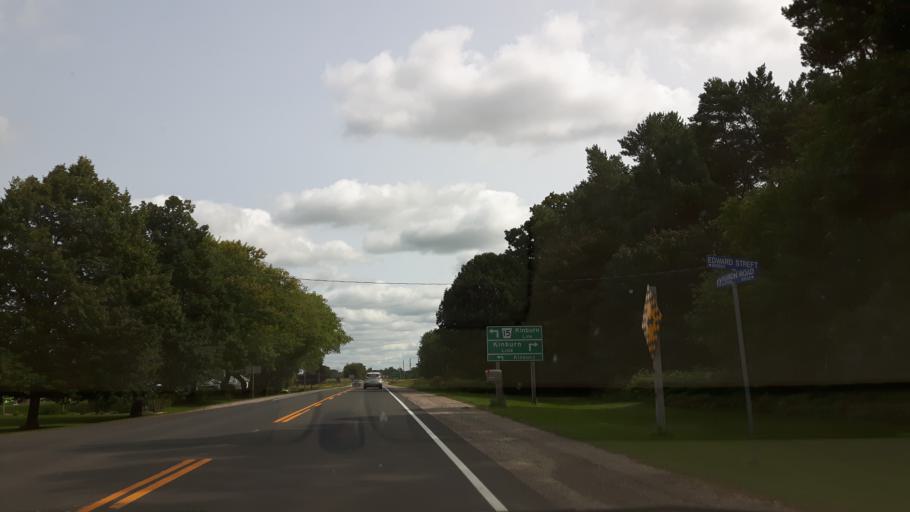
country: CA
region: Ontario
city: Huron East
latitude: 43.5835
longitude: -81.4622
